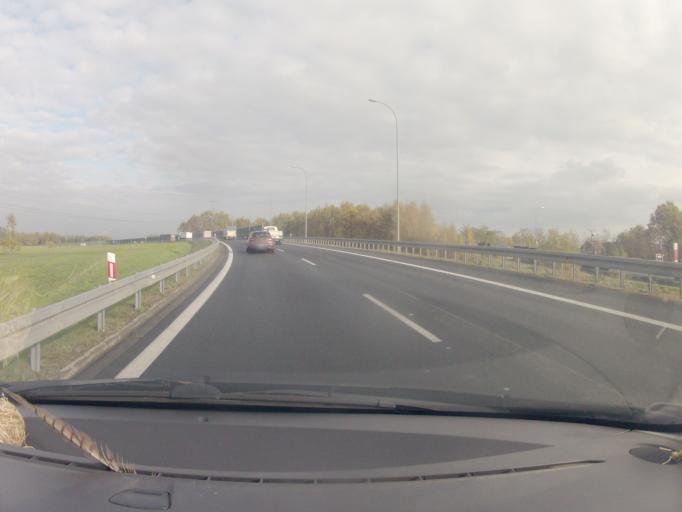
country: PL
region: Lesser Poland Voivodeship
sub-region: Powiat wielicki
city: Czarnochowice
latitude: 50.0114
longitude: 20.0655
